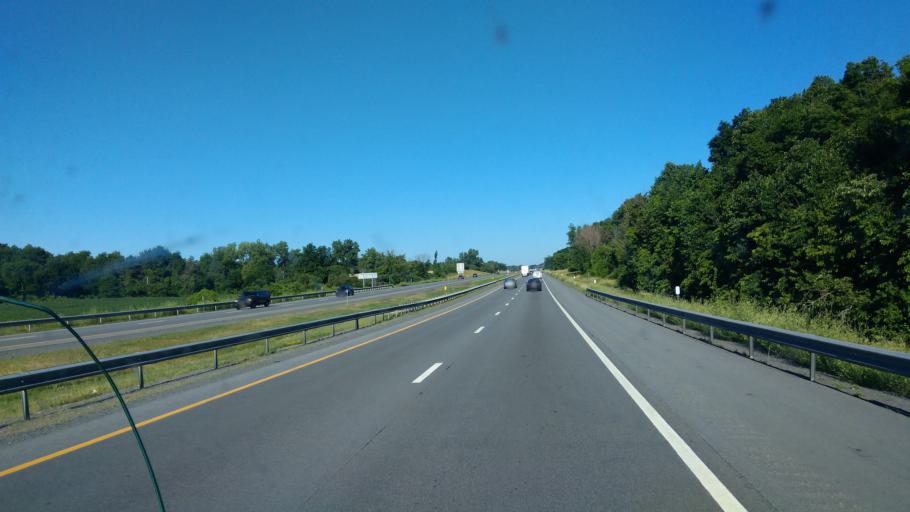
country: US
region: New York
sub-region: Monroe County
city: Scottsville
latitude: 43.0453
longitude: -77.7542
